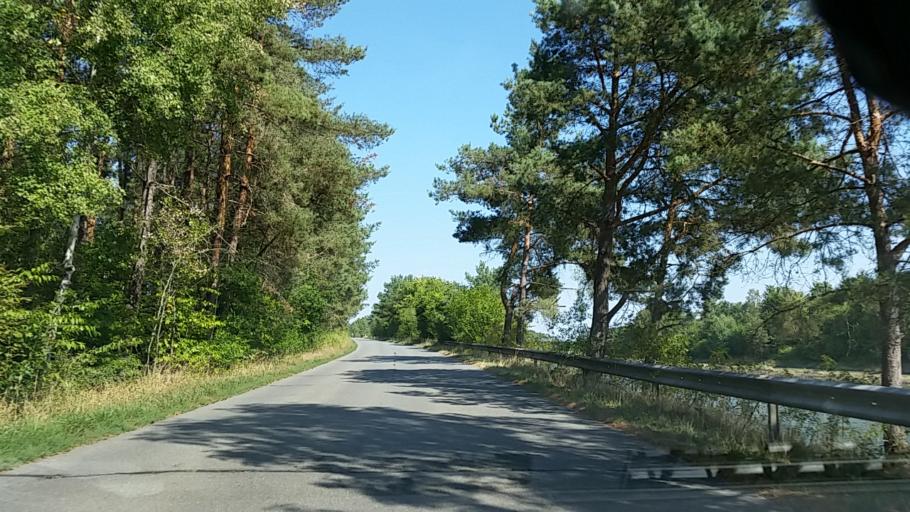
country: DE
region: Lower Saxony
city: Emmendorf
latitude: 53.0094
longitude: 10.5696
